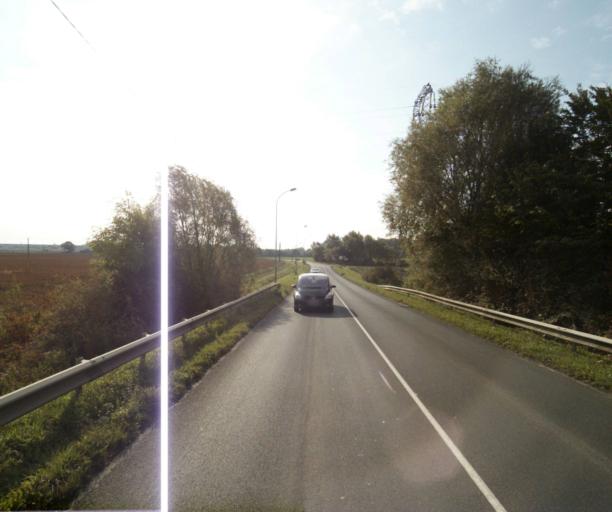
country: FR
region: Nord-Pas-de-Calais
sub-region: Departement du Nord
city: Lompret
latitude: 50.6590
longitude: 2.9921
